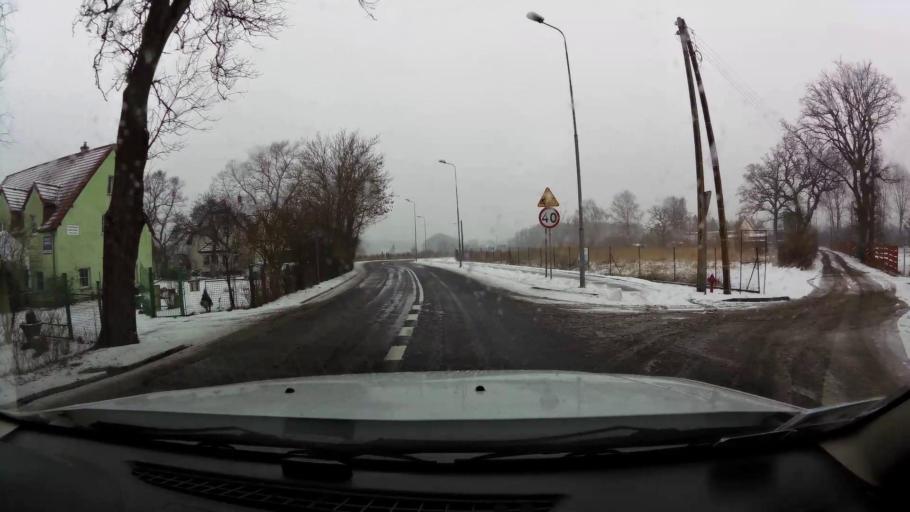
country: PL
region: West Pomeranian Voivodeship
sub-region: Powiat gryficki
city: Mrzezyno
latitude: 54.1350
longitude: 15.2842
